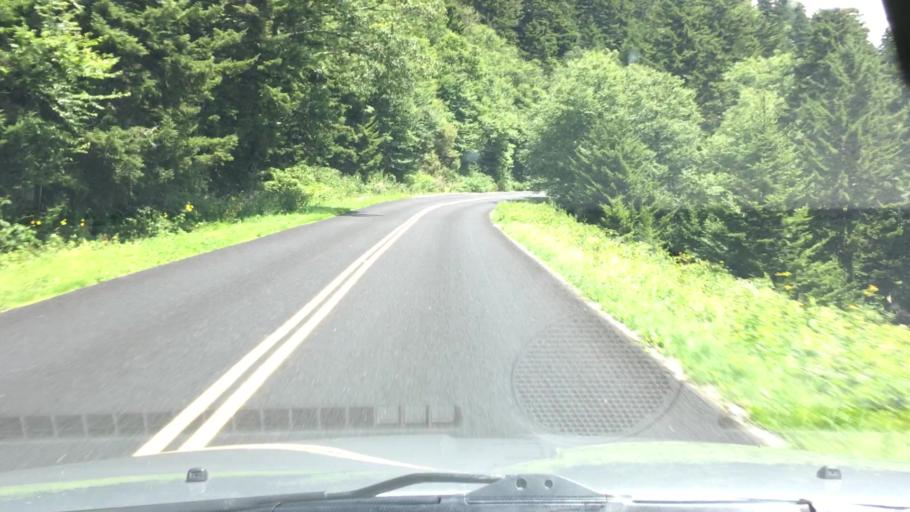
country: US
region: North Carolina
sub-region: Buncombe County
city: Black Mountain
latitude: 35.7452
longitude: -82.3305
